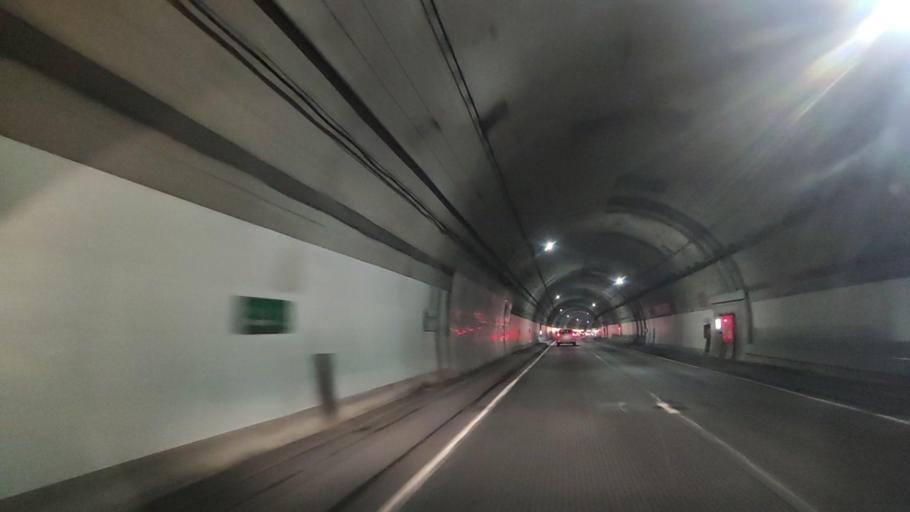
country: JP
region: Hokkaido
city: Rumoi
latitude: 43.7038
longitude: 141.3360
